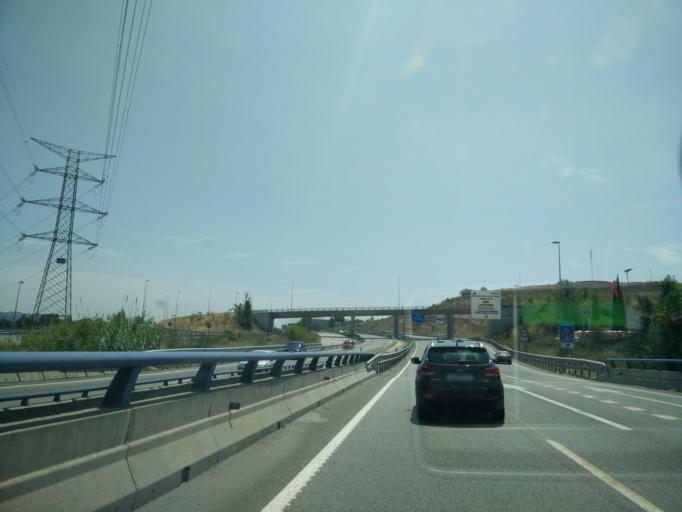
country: ES
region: Catalonia
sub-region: Provincia de Barcelona
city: Abrera
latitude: 41.5239
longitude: 1.8842
